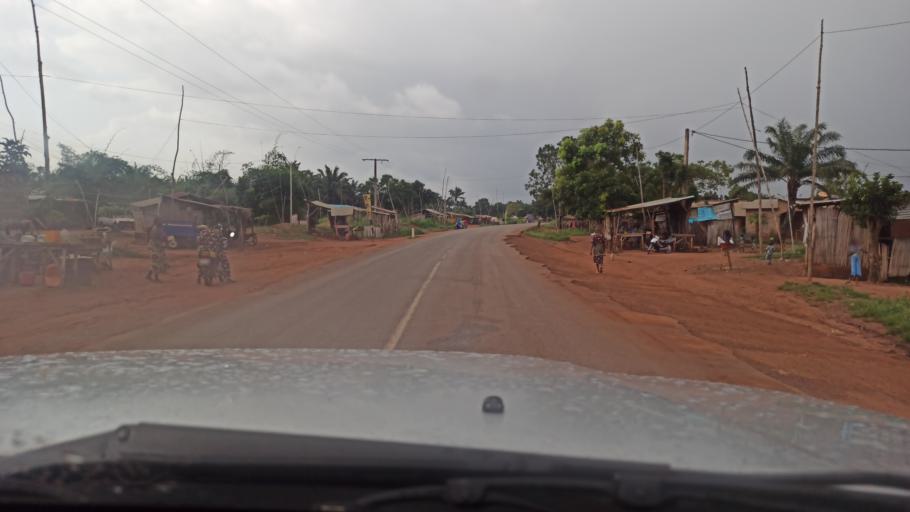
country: BJ
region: Queme
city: Porto-Novo
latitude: 6.5622
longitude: 2.5824
